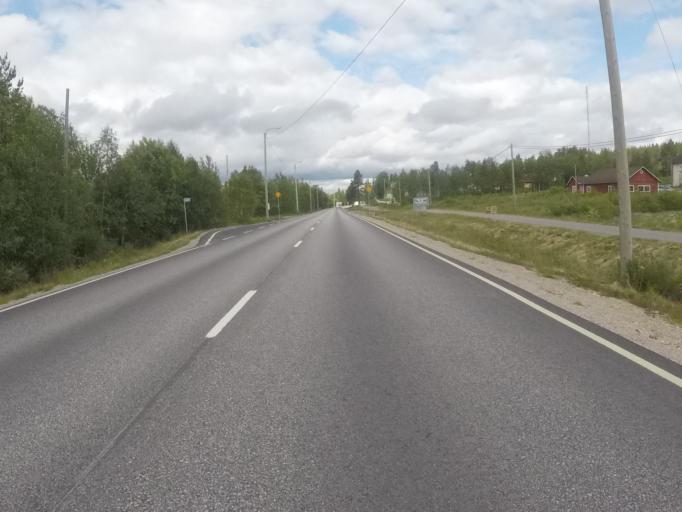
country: FI
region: Lapland
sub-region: Tunturi-Lappi
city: Enontekioe
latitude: 68.2786
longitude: 23.0864
